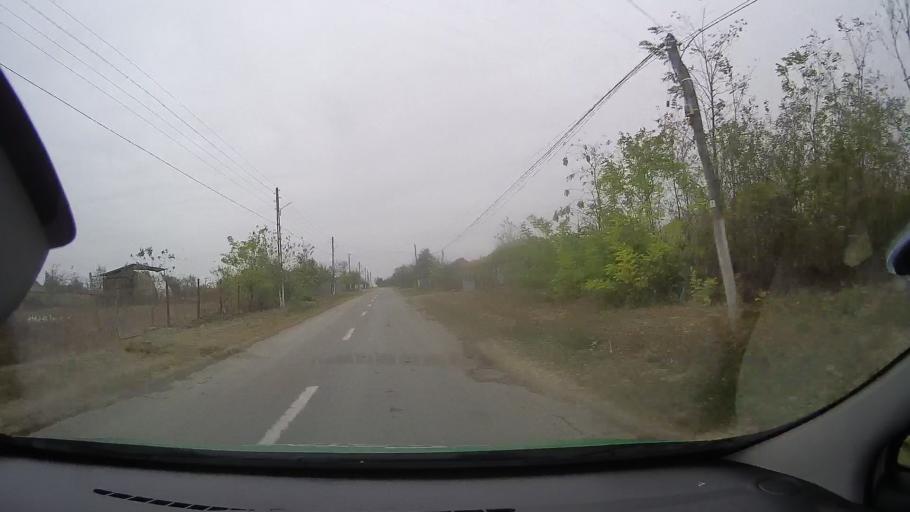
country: RO
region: Constanta
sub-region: Comuna Vulturu
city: Vulturu
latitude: 44.6512
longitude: 28.2682
